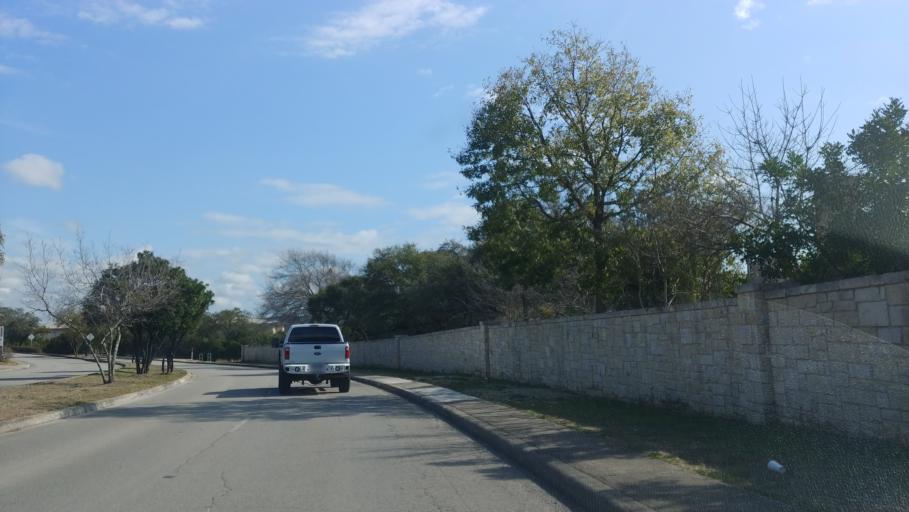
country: US
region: Texas
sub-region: Bexar County
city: Cross Mountain
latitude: 29.6174
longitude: -98.6130
